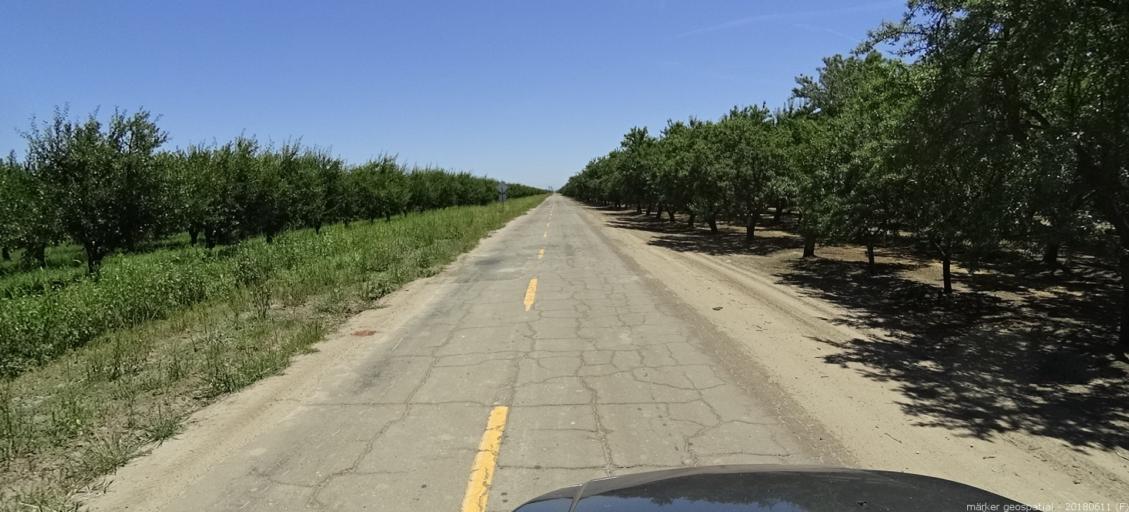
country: US
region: California
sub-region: Madera County
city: Fairmead
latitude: 37.0547
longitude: -120.2188
